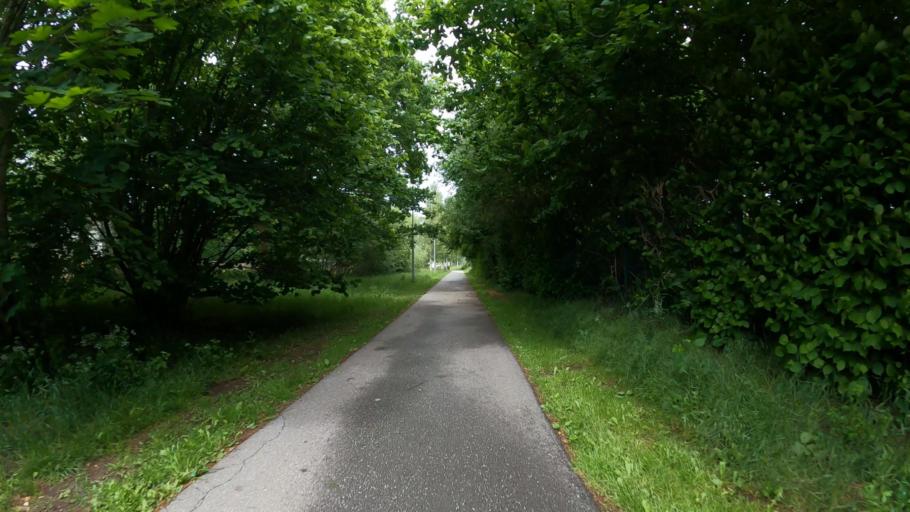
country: DE
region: Schleswig-Holstein
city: Norderstedt
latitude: 53.7176
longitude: 9.9921
